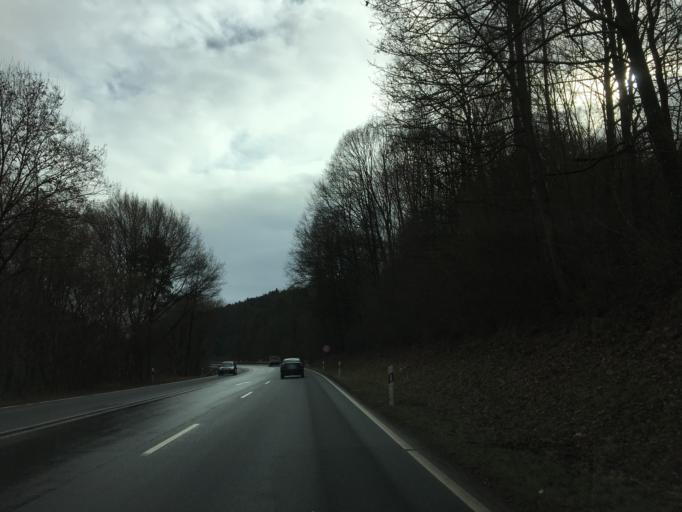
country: DE
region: Hesse
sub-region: Regierungsbezirk Darmstadt
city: Bad Konig
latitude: 49.7155
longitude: 8.9906
